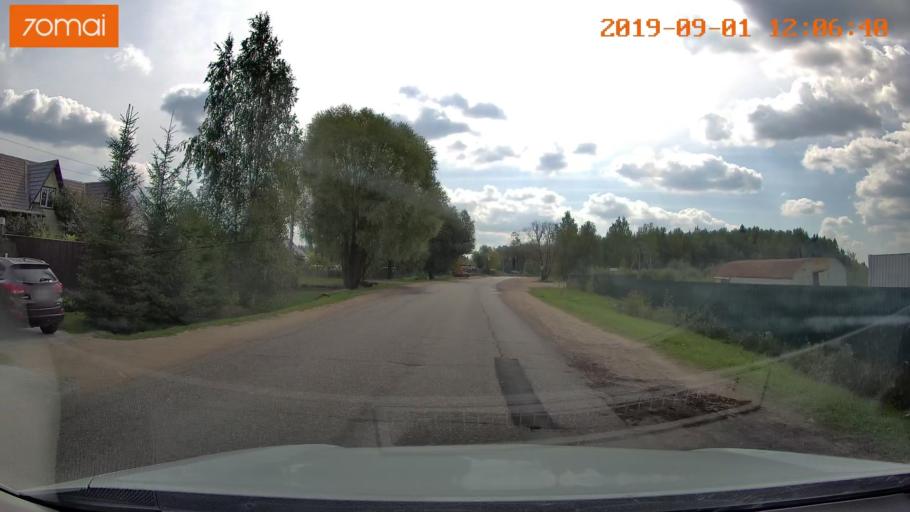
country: RU
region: Kaluga
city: Maloyaroslavets
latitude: 54.9870
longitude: 36.4712
